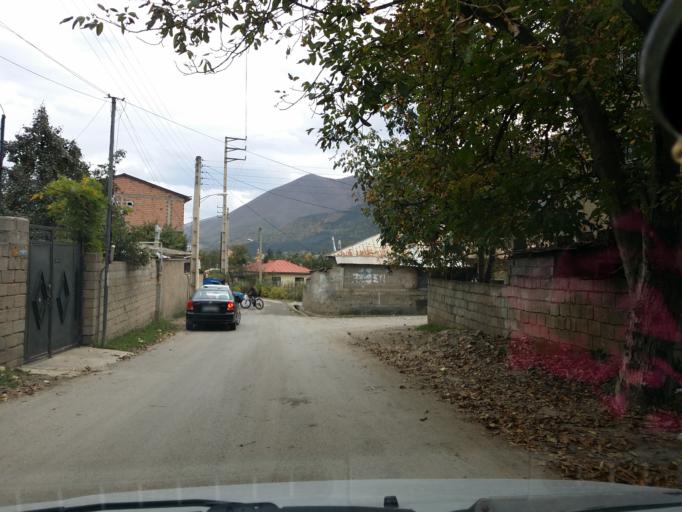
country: IR
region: Mazandaran
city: `Abbasabad
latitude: 36.5043
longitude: 51.1474
